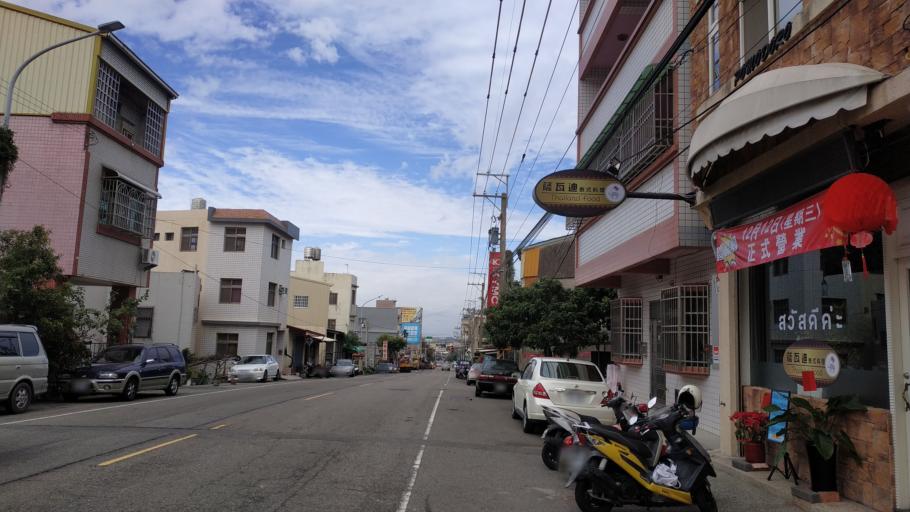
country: TW
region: Taiwan
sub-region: Taichung City
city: Taichung
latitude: 24.2135
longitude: 120.5802
